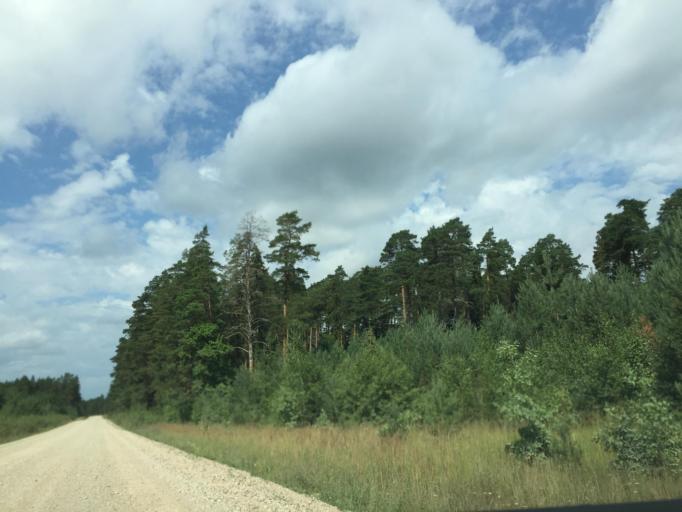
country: LV
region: Kandava
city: Kandava
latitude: 57.0306
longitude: 22.8142
